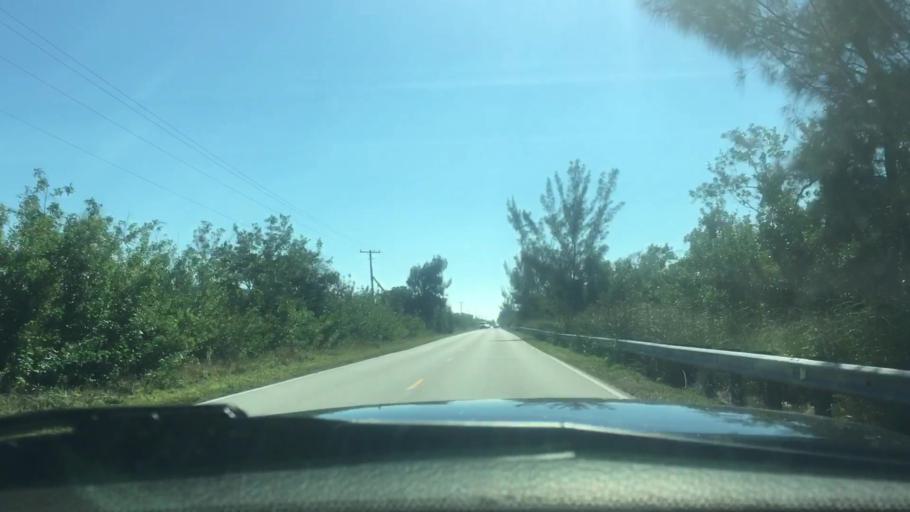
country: US
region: Florida
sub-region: Miami-Dade County
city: Florida City
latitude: 25.3629
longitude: -80.4272
